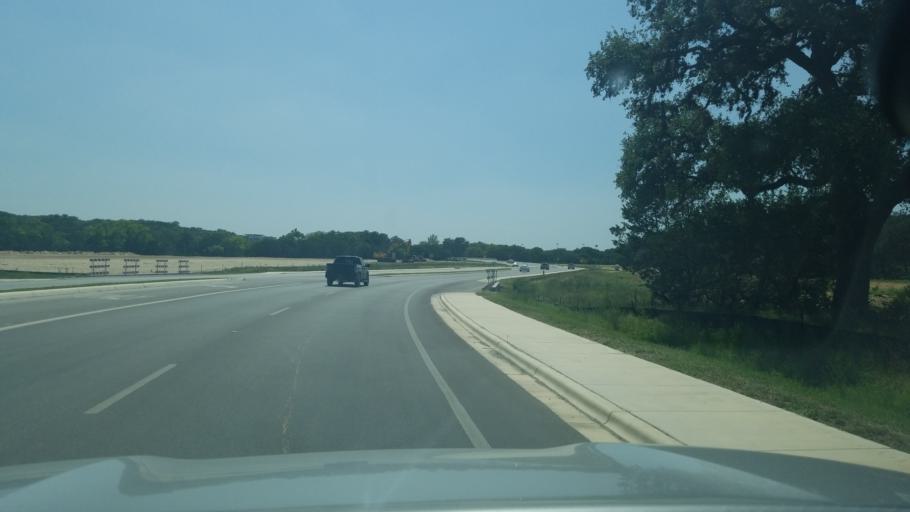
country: US
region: Texas
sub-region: Kendall County
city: Boerne
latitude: 29.7766
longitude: -98.7186
